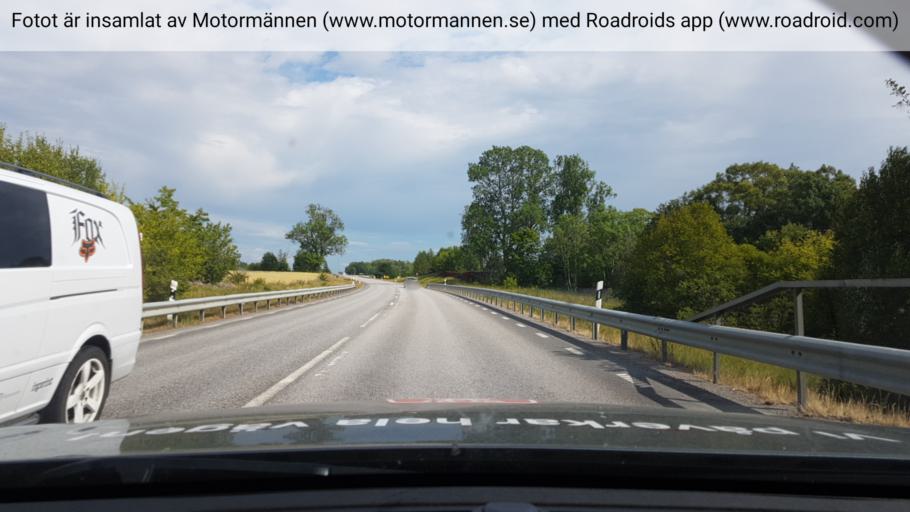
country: SE
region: Uppsala
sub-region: Enkopings Kommun
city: Orsundsbro
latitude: 59.8543
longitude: 17.4349
